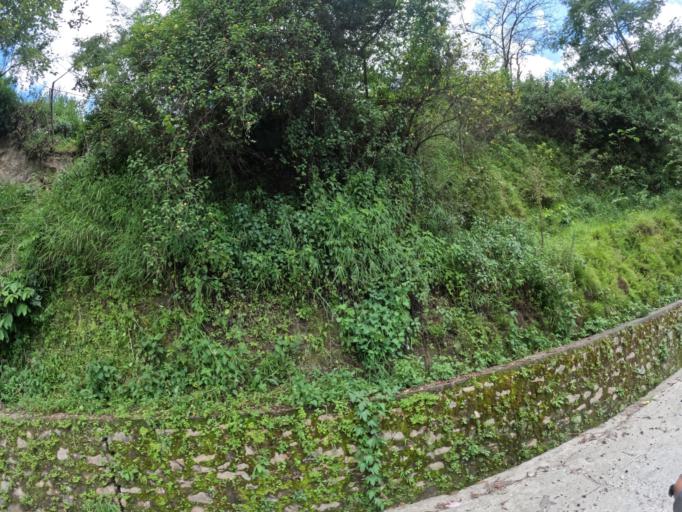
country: NP
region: Central Region
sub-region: Bagmati Zone
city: Kathmandu
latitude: 27.8009
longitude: 85.3289
